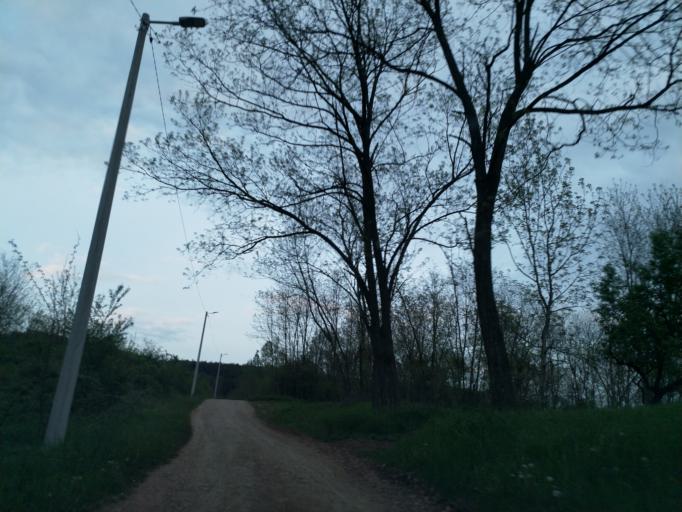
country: RS
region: Central Serbia
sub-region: Pomoravski Okrug
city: Paracin
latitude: 43.9422
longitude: 21.5094
